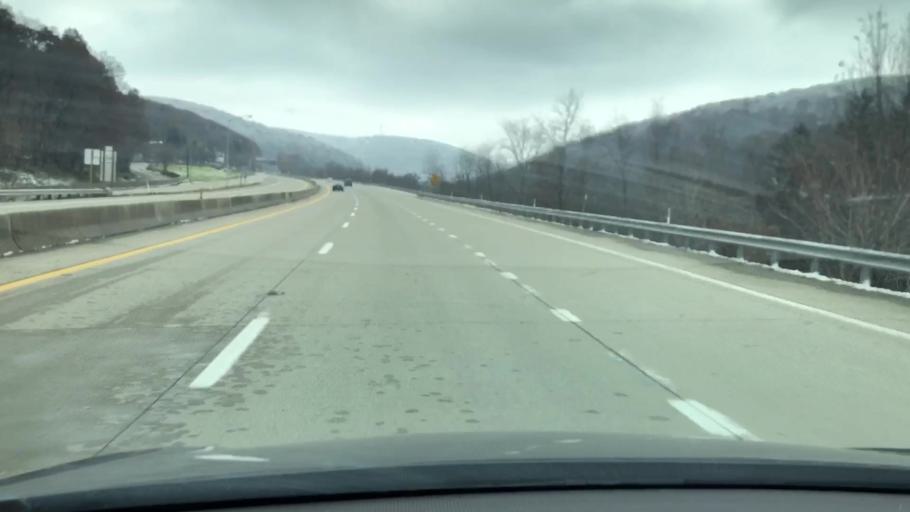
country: US
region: Pennsylvania
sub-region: Fayette County
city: Hopwood
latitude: 39.8690
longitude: -79.6966
